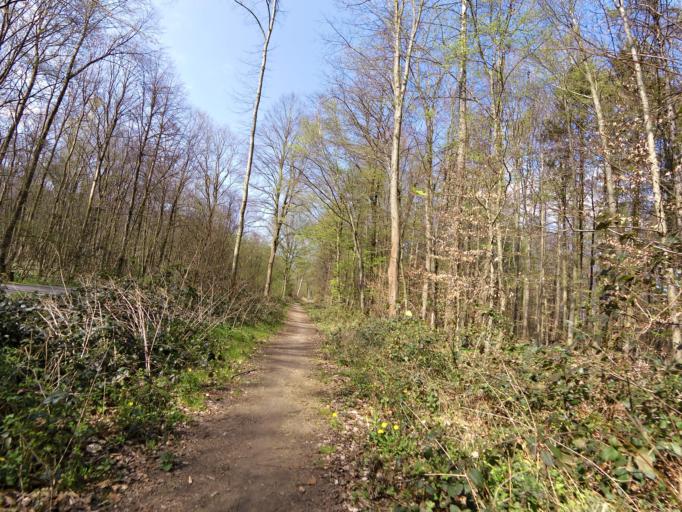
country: DE
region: North Rhine-Westphalia
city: Meckenheim
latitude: 50.6674
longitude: 7.0189
